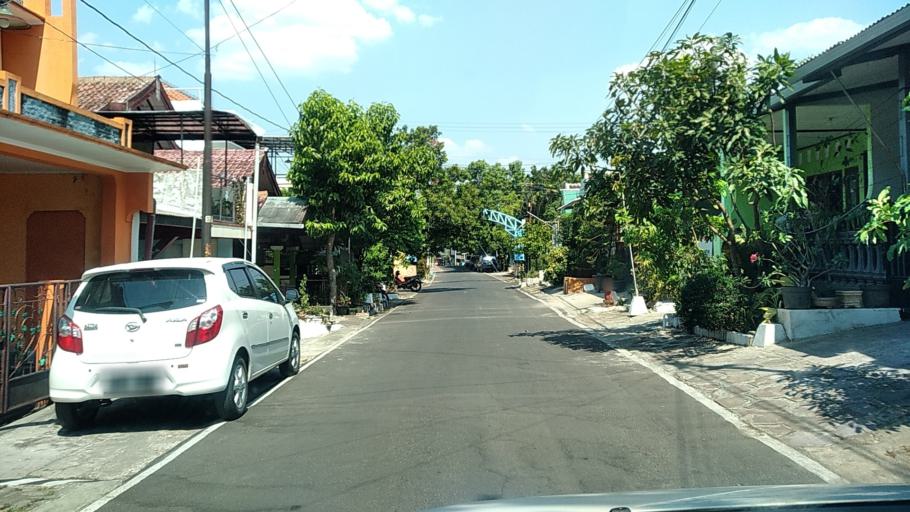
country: ID
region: Central Java
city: Ungaran
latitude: -7.0742
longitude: 110.4317
